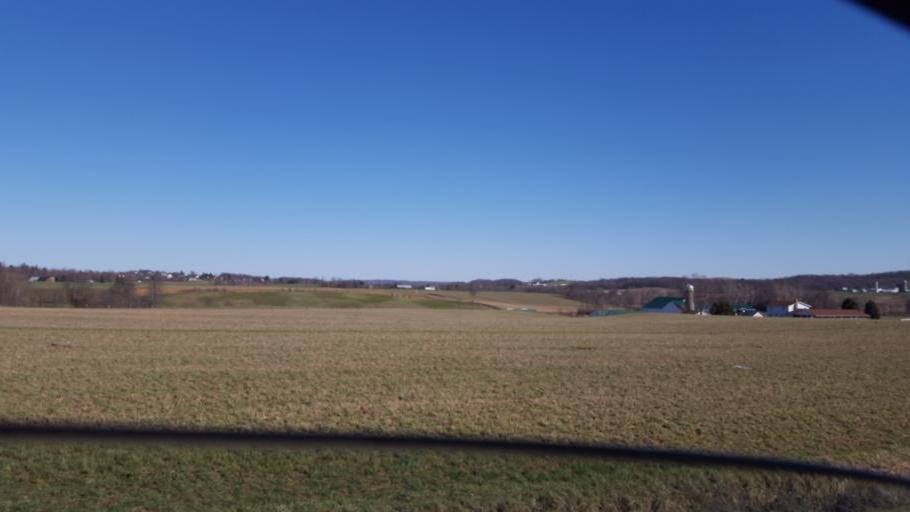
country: US
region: Ohio
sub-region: Wayne County
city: Dalton
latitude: 40.7253
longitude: -81.6953
